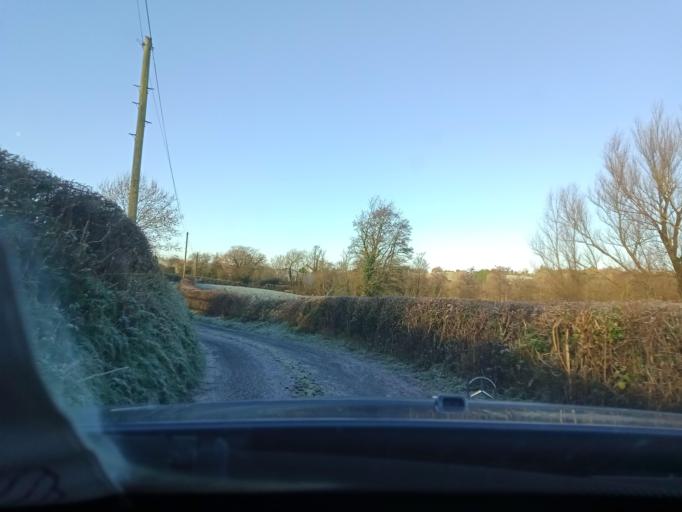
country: IE
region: Leinster
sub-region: Kilkenny
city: Graiguenamanagh
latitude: 52.5980
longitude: -6.9504
